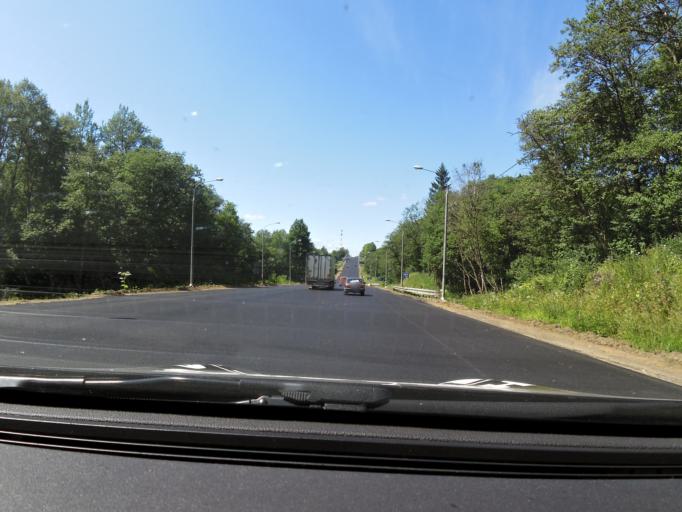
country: RU
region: Novgorod
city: Valday
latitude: 57.9505
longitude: 33.3062
